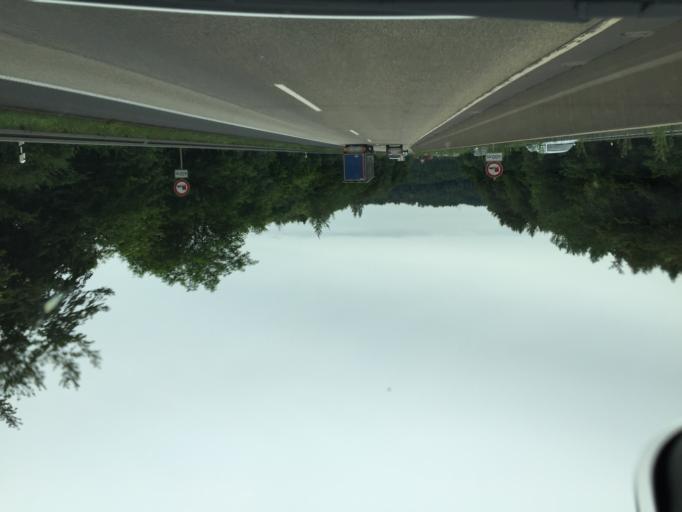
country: DE
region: Bavaria
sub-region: Regierungsbezirk Unterfranken
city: Motten
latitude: 50.3607
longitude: 9.7343
